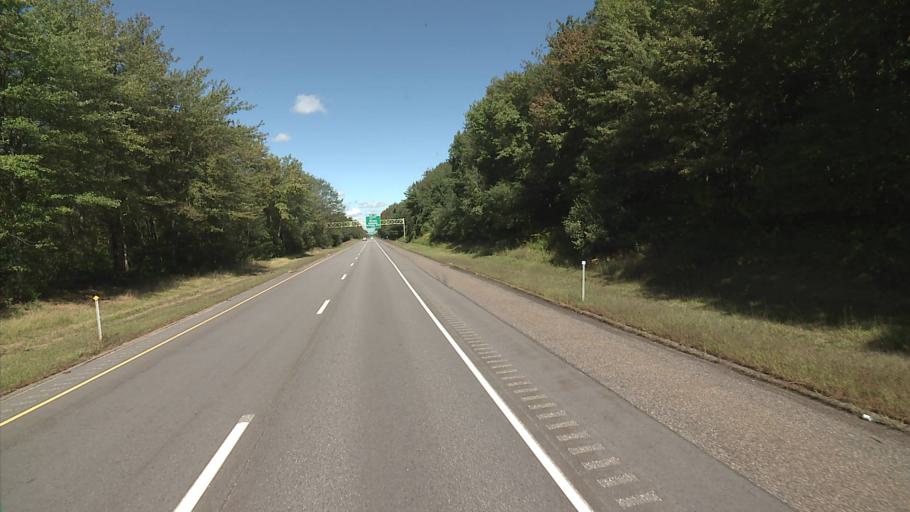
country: US
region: Connecticut
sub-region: New London County
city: Colchester
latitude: 41.5404
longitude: -72.3129
